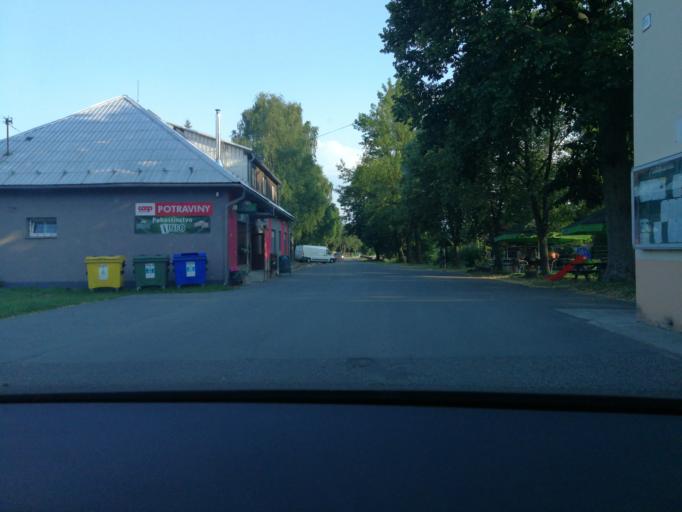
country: SK
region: Zilinsky
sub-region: Okres Liptovsky Mikulas
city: Liptovsky Mikulas
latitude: 49.1677
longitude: 19.5424
